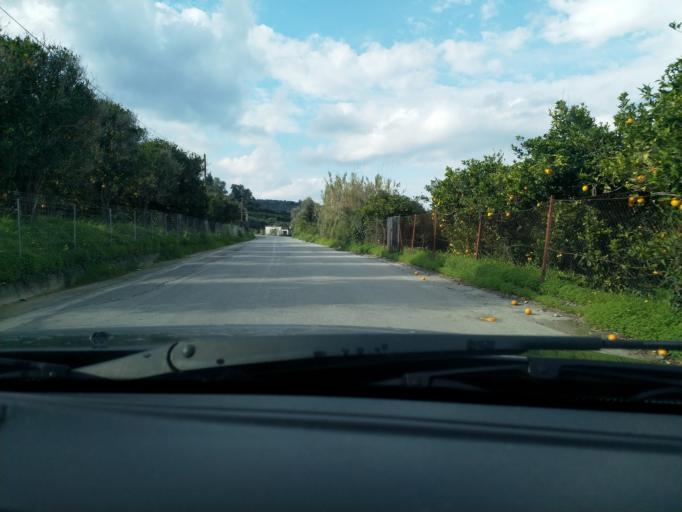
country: GR
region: Crete
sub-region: Nomos Chanias
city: Gerani
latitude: 35.4997
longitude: 23.8994
